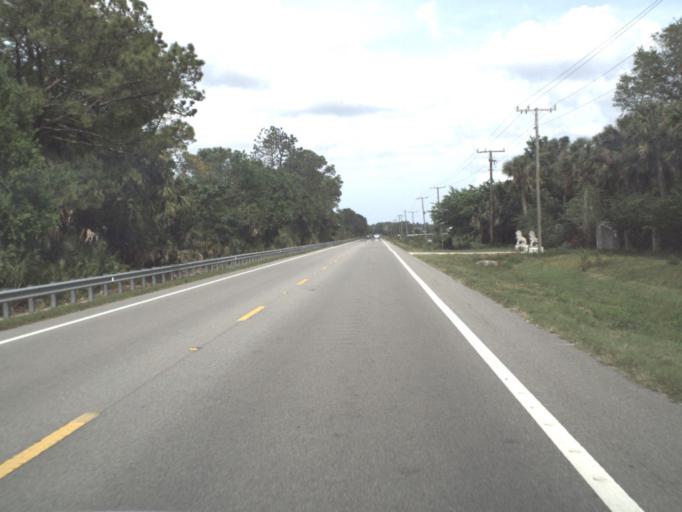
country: US
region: Florida
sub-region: Flagler County
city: Bunnell
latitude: 29.4819
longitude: -81.3692
